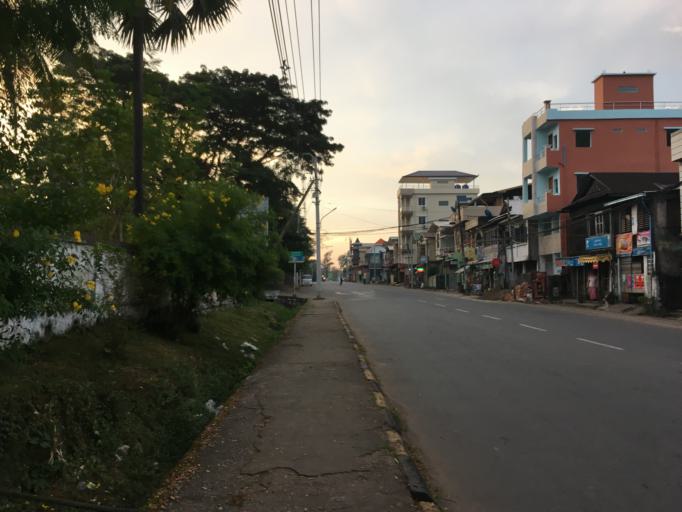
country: MM
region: Mon
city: Mawlamyine
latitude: 16.4707
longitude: 97.6256
